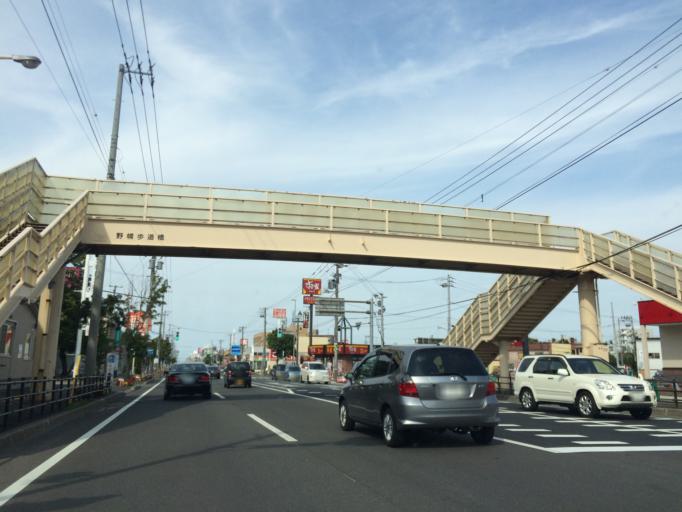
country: JP
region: Hokkaido
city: Ebetsu
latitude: 43.0935
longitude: 141.5242
